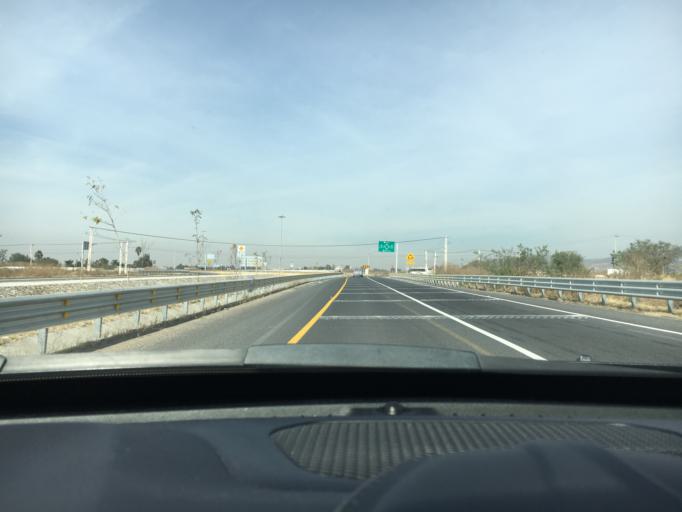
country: MX
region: Guanajuato
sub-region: Leon
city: Ladrilleras del Refugio
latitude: 21.0762
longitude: -101.5431
